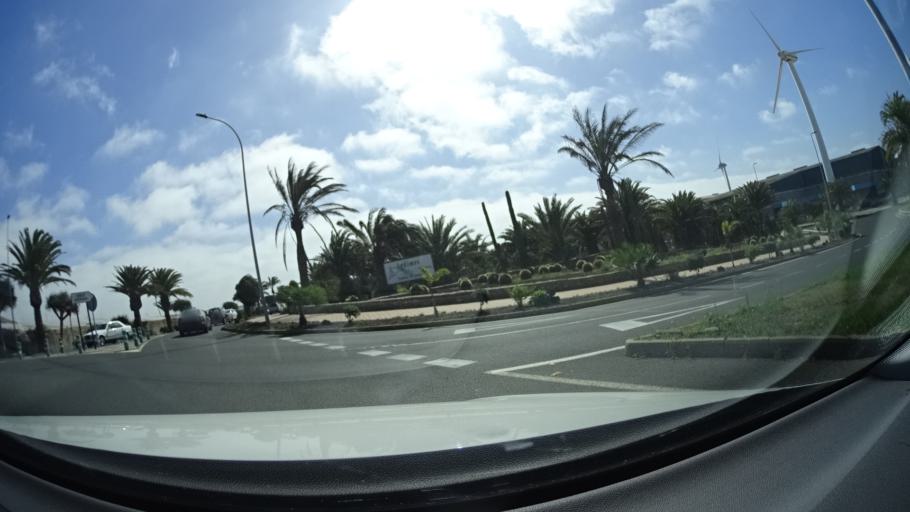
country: ES
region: Canary Islands
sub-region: Provincia de Las Palmas
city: Cruce de Arinaga
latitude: 27.8629
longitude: -15.4057
